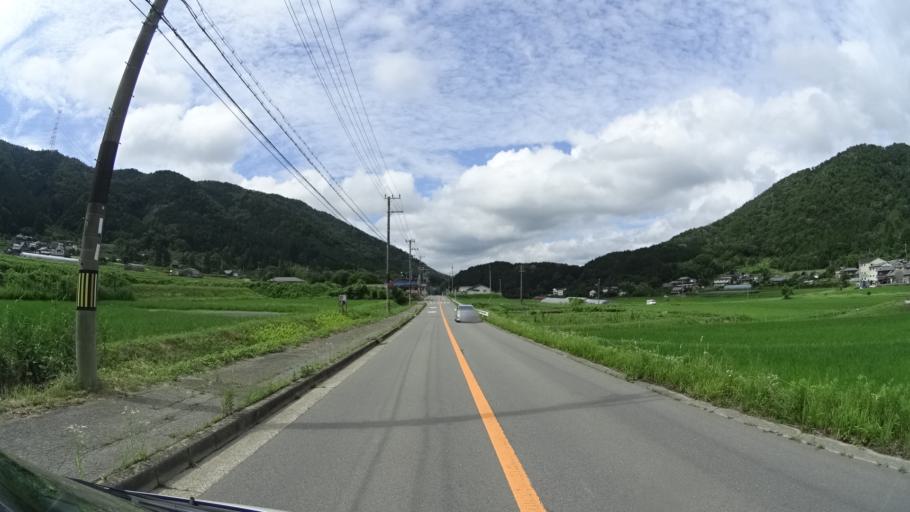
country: JP
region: Kyoto
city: Kameoka
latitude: 34.9889
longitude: 135.4761
